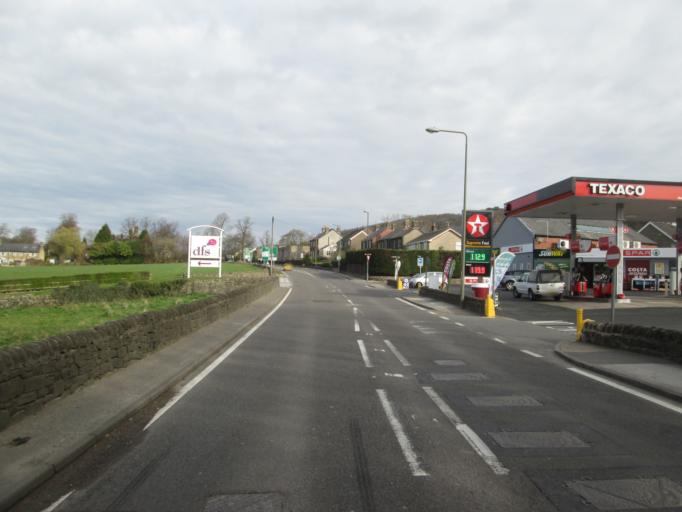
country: GB
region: England
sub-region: Derbyshire
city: Matlock
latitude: 53.1605
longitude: -1.5872
